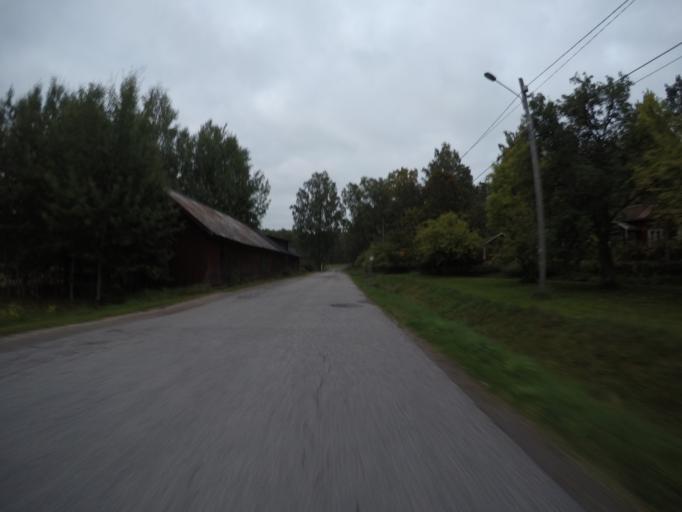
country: SE
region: Vaestmanland
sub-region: Kungsors Kommun
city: Kungsoer
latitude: 59.4078
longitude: 16.1133
